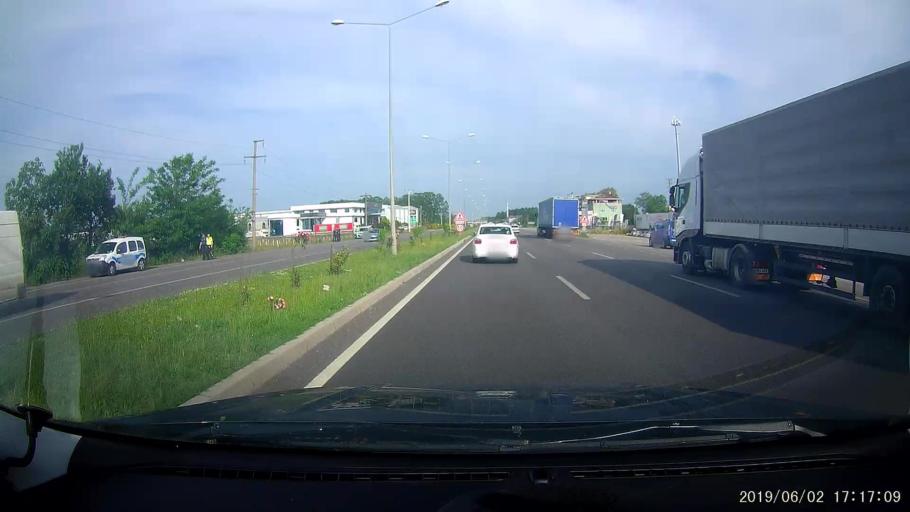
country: TR
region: Samsun
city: Dikbiyik
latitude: 41.2308
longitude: 36.5768
